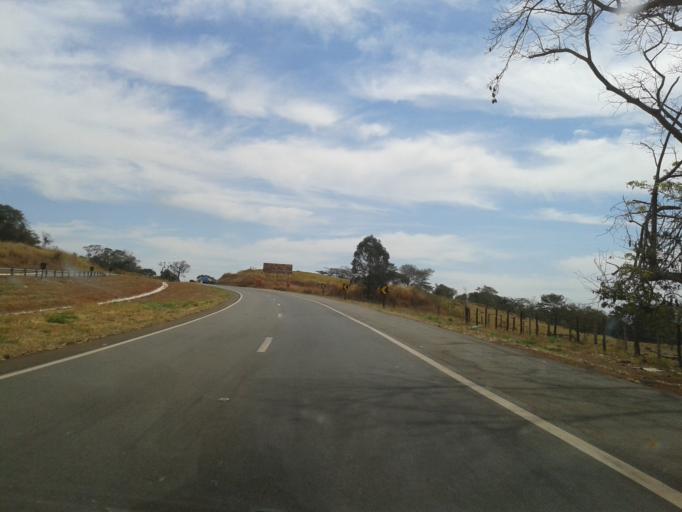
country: BR
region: Goias
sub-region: Itaberai
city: Itaberai
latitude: -16.1488
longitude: -49.6327
